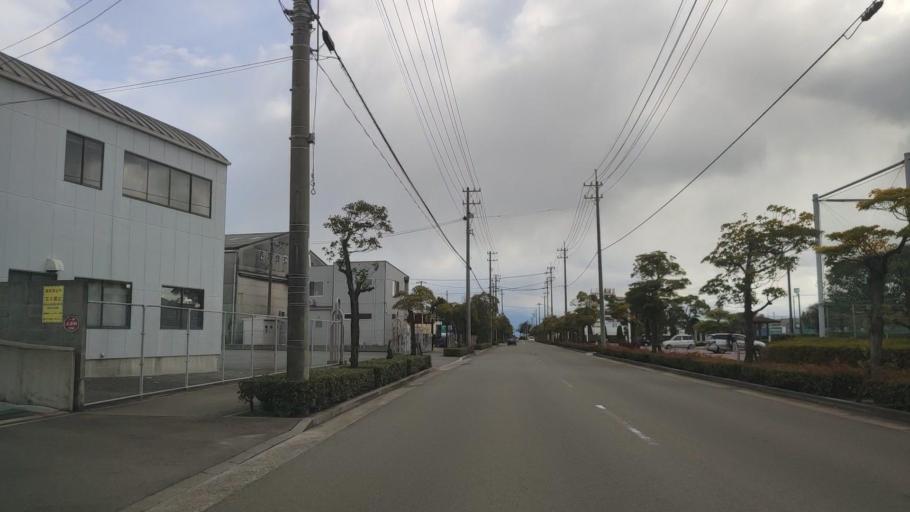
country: JP
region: Ehime
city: Saijo
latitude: 34.0488
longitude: 133.0263
